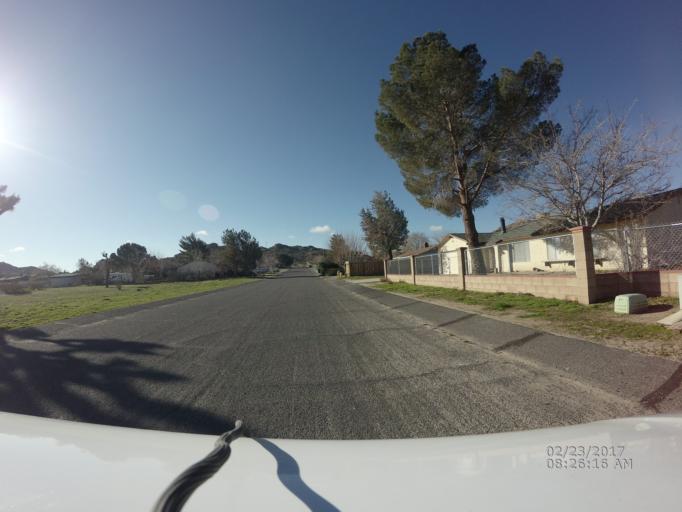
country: US
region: California
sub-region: Los Angeles County
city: Lake Los Angeles
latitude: 34.6124
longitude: -117.8296
